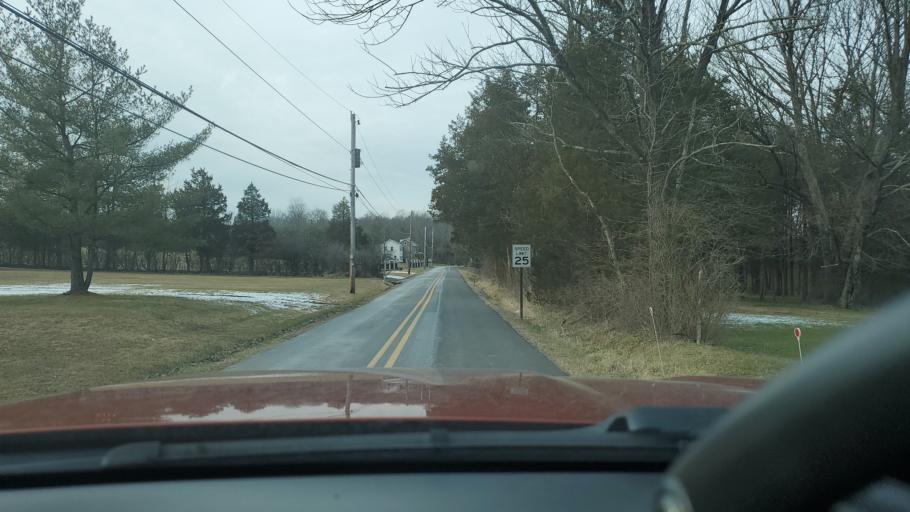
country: US
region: Pennsylvania
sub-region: Montgomery County
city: Woxall
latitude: 40.3137
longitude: -75.4963
